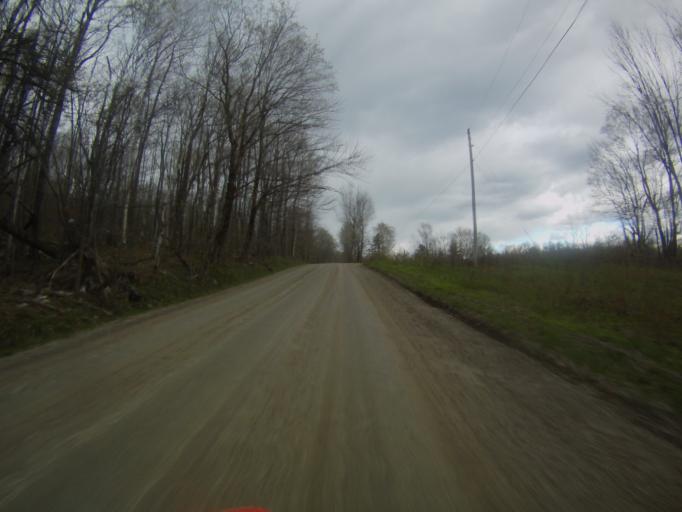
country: US
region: Vermont
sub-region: Addison County
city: Bristol
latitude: 44.0600
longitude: -73.0307
